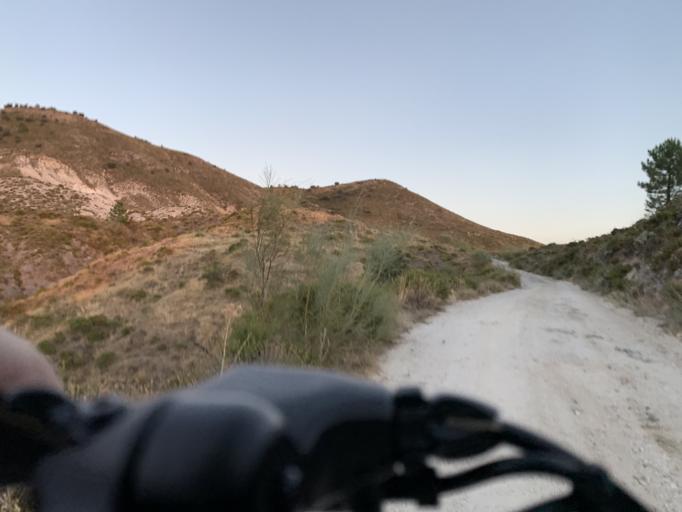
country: ES
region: Andalusia
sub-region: Provincia de Granada
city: Beas de Granada
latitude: 37.2266
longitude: -3.4630
